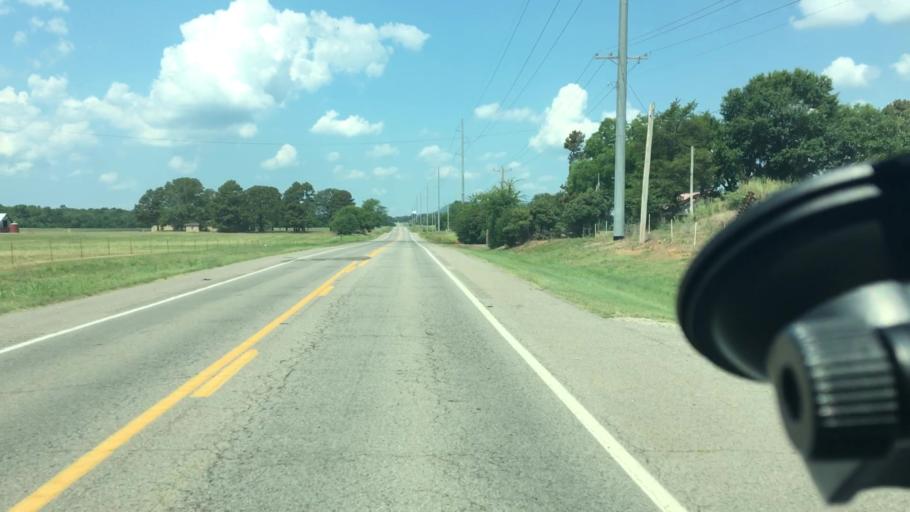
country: US
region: Arkansas
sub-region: Logan County
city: Paris
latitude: 35.2948
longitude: -93.6642
